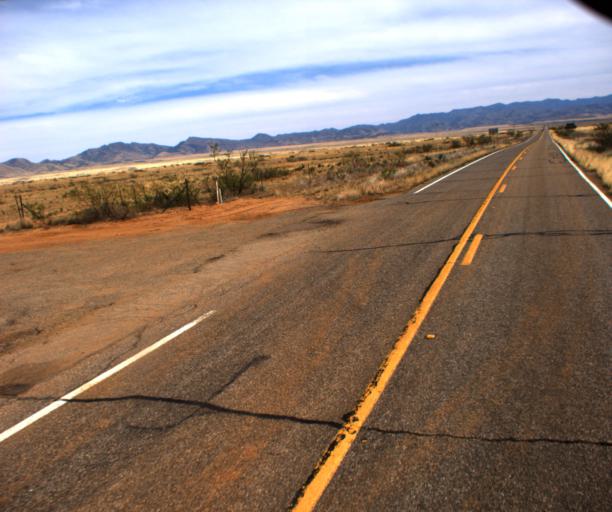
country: US
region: Arizona
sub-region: Cochise County
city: Willcox
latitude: 32.0940
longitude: -109.5347
